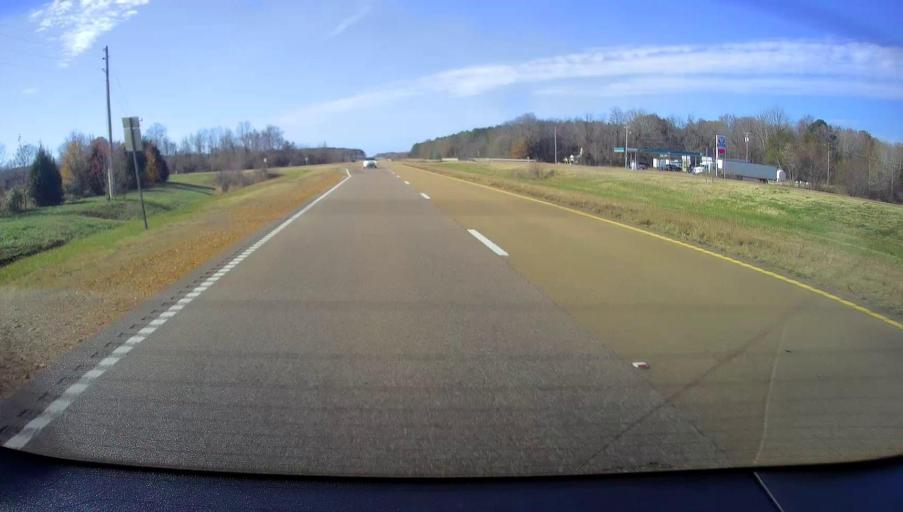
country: US
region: Mississippi
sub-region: Benton County
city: Ashland
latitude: 34.9461
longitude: -89.2093
